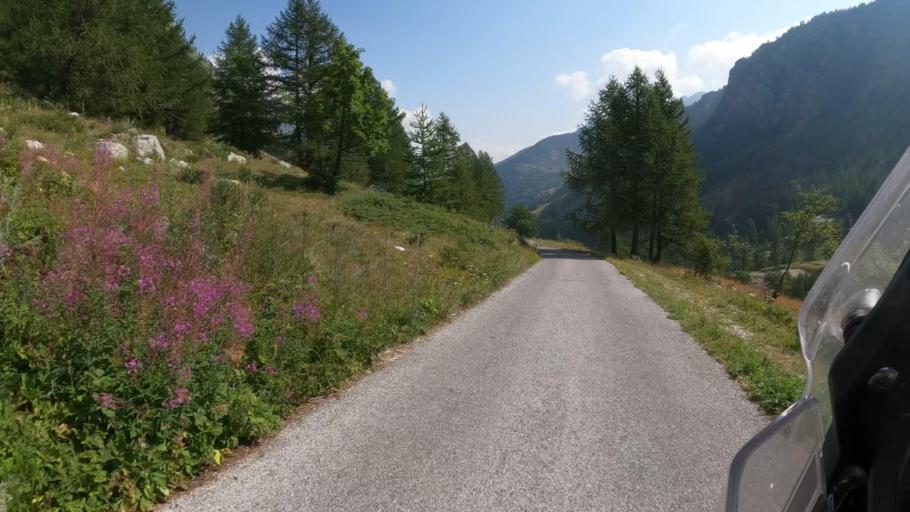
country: IT
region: Piedmont
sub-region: Provincia di Cuneo
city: Canosio
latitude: 44.4144
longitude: 7.0414
